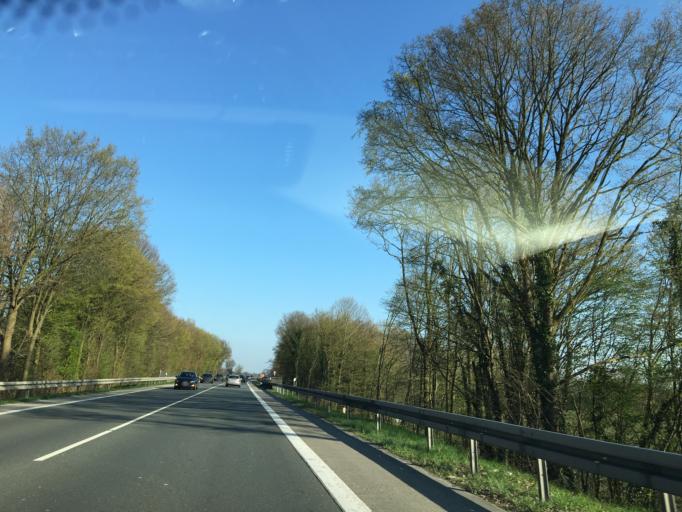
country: DE
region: North Rhine-Westphalia
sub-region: Regierungsbezirk Munster
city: Greven
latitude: 52.0803
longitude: 7.6507
